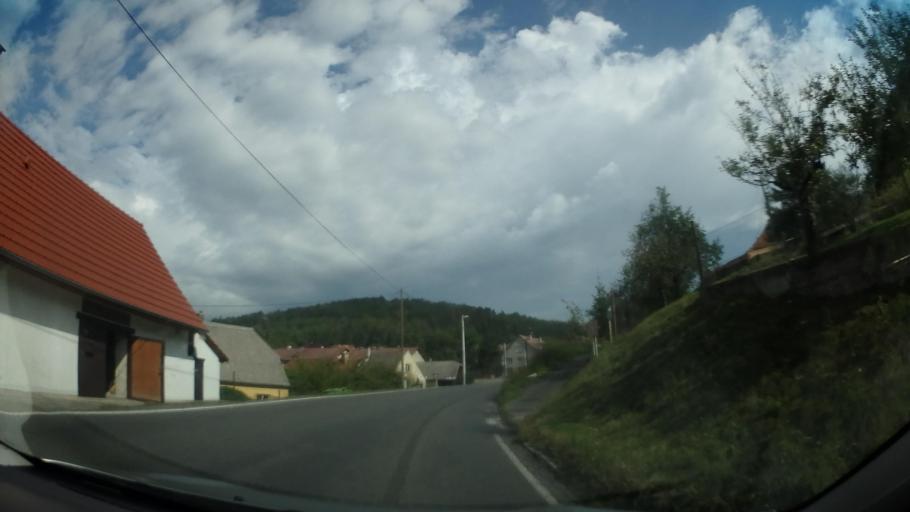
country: CZ
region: Plzensky
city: Horazd'ovice
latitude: 49.2791
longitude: 13.6149
